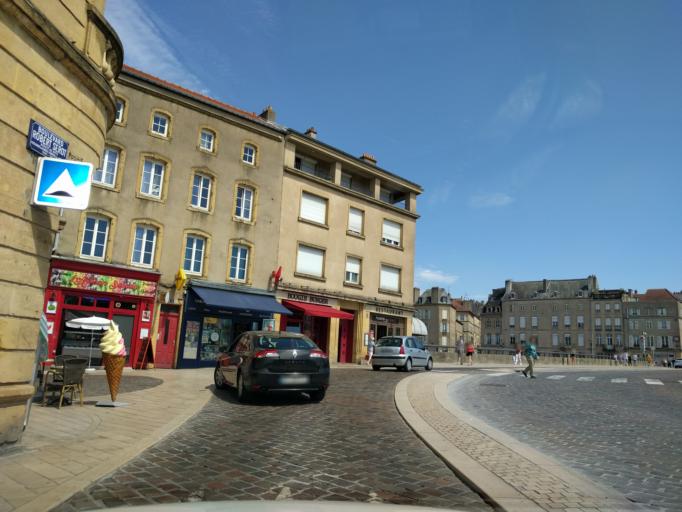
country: FR
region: Lorraine
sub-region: Departement de la Moselle
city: Metz
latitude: 49.1199
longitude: 6.1699
